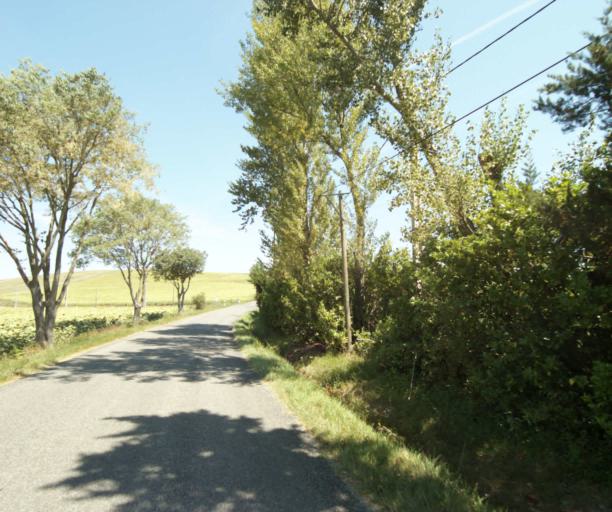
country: FR
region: Midi-Pyrenees
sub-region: Departement de l'Ariege
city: Lezat-sur-Leze
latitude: 43.2901
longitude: 1.3549
